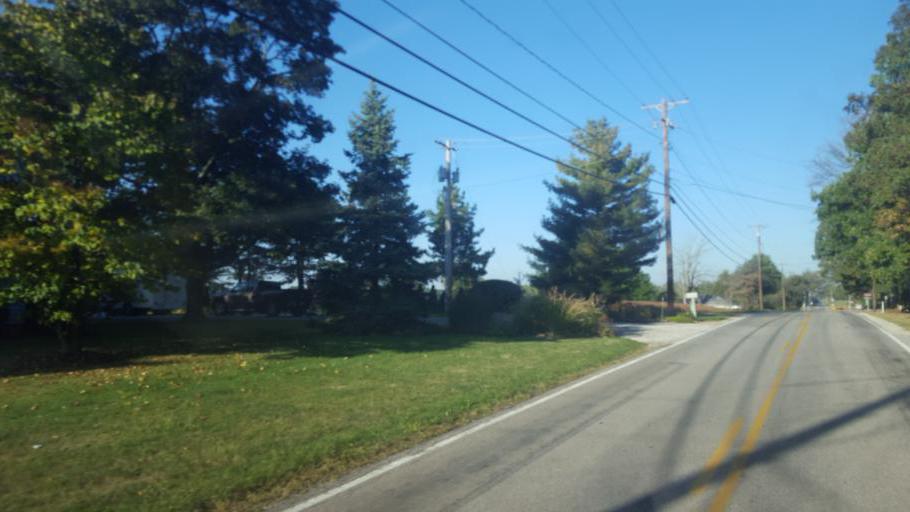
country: US
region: Ohio
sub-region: Marion County
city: Marion
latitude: 40.5494
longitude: -83.1246
